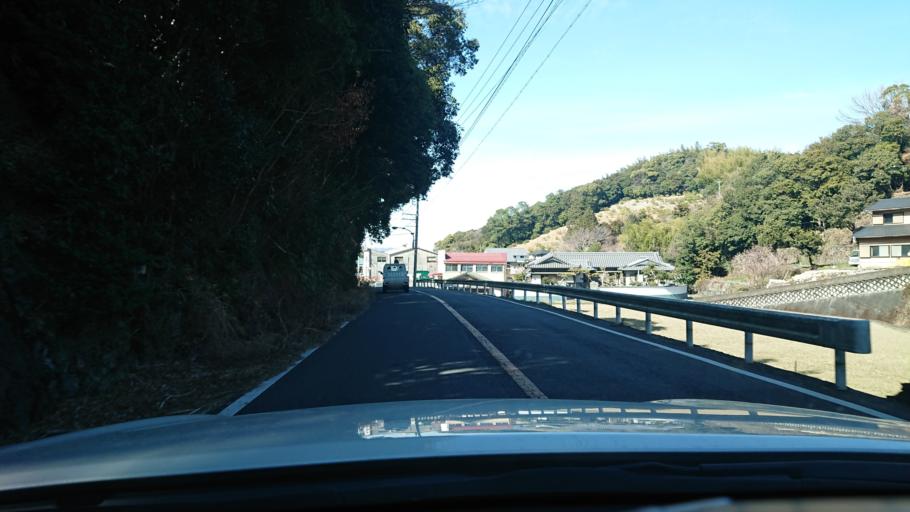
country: JP
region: Tokushima
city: Komatsushimacho
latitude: 33.9722
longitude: 134.5924
